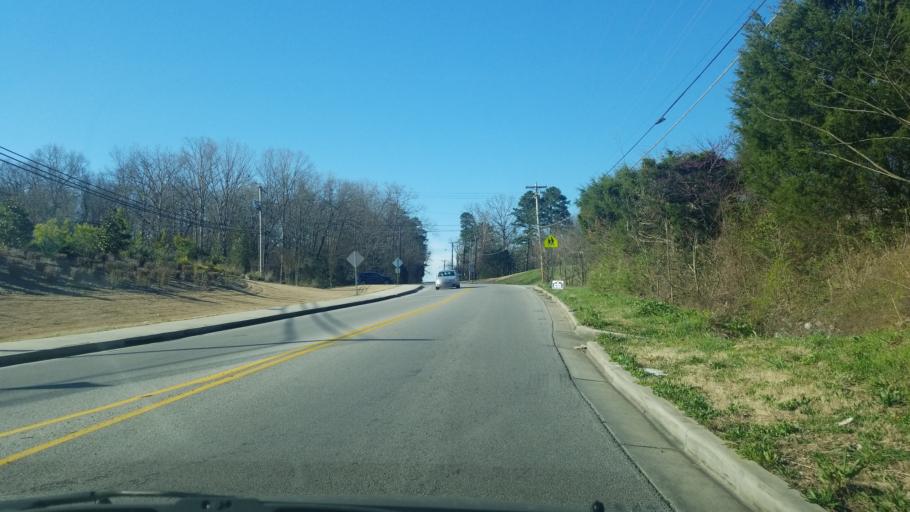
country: US
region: Tennessee
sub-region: Hamilton County
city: East Brainerd
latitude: 35.0494
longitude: -85.1451
